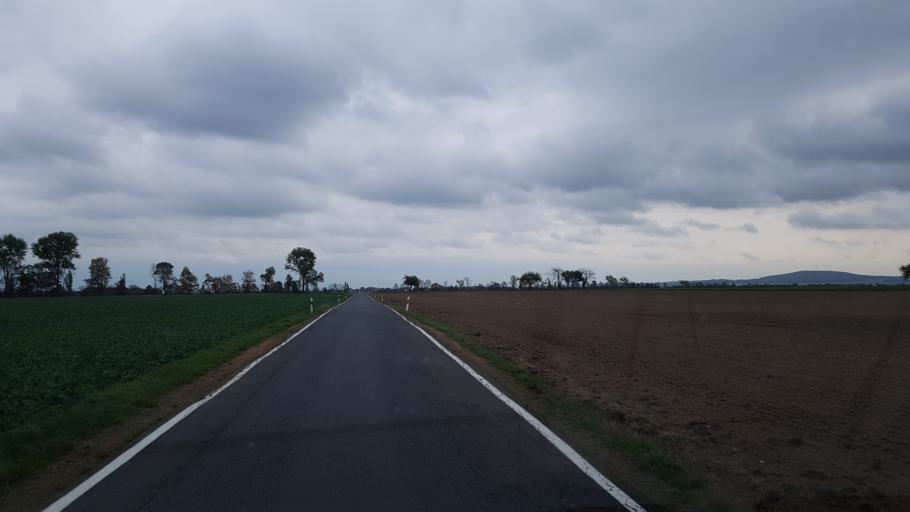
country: DE
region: Saxony
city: Dahlen
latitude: 51.3769
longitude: 12.9597
